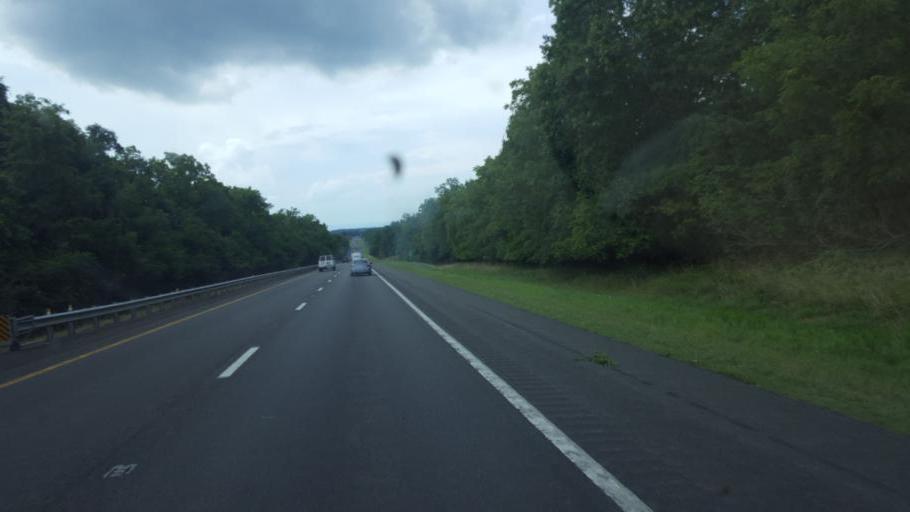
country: US
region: Virginia
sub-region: Warren County
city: Front Royal
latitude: 38.9479
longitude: -78.1552
